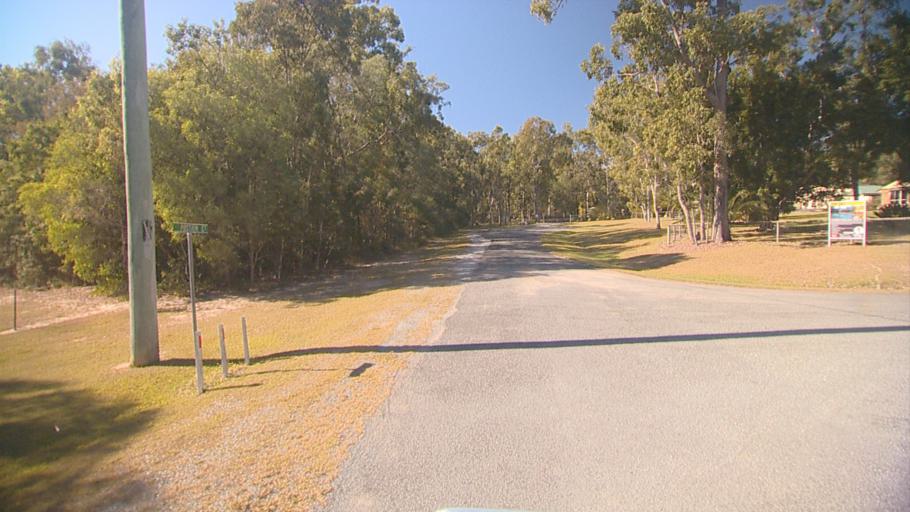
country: AU
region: Queensland
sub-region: Logan
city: Chambers Flat
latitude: -27.7821
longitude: 153.1034
